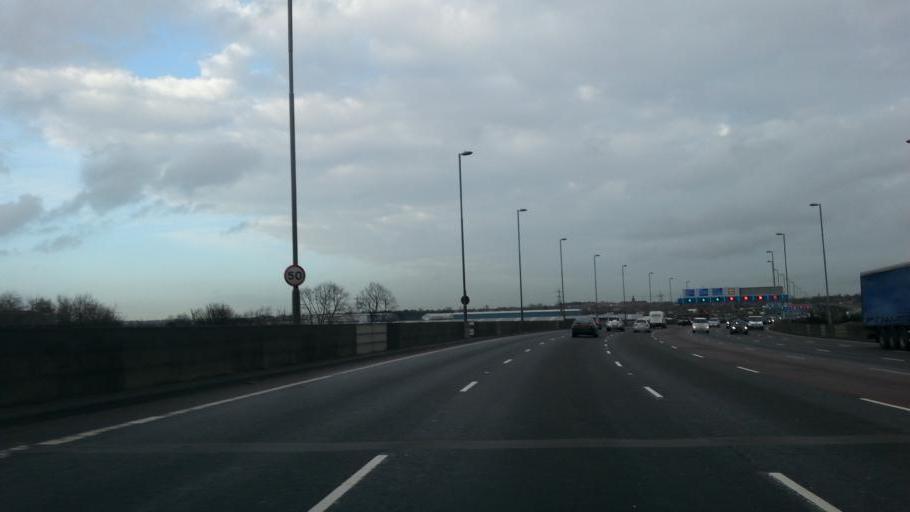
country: GB
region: England
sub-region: City and Borough of Birmingham
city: Birmingham
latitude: 52.5059
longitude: -1.8796
